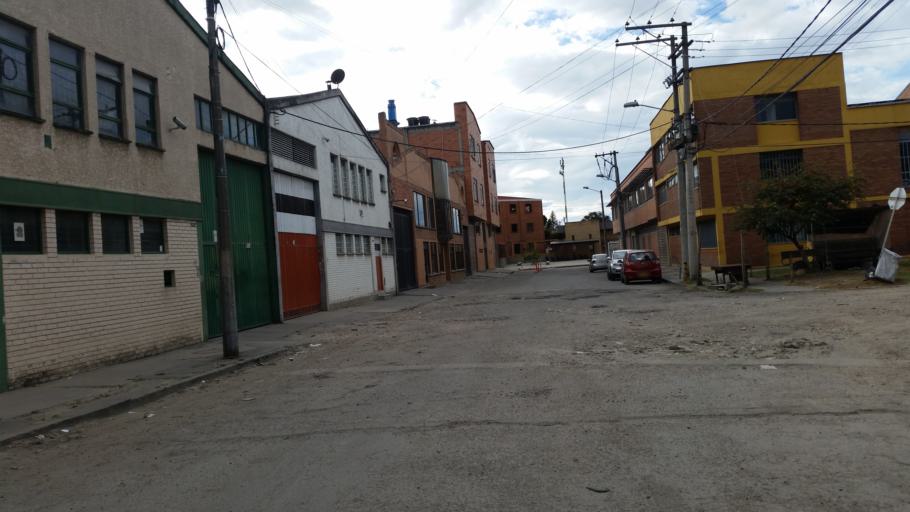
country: CO
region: Bogota D.C.
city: Bogota
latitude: 4.6300
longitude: -74.0996
